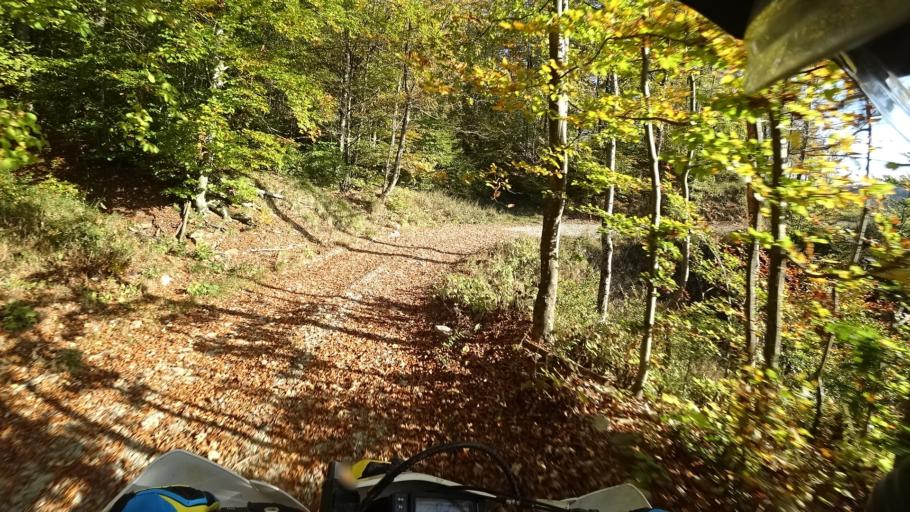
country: HR
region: Primorsko-Goranska
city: Klana
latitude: 45.4921
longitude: 14.4069
